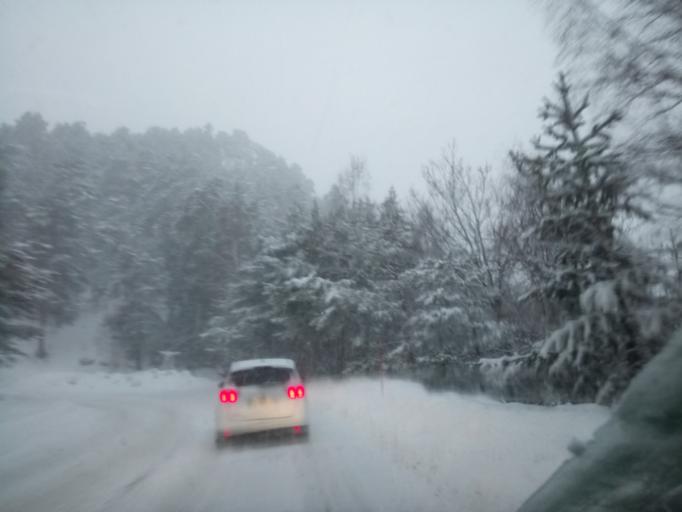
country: FR
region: Rhone-Alpes
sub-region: Departement de la Savoie
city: Modane
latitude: 45.2045
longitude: 6.7022
